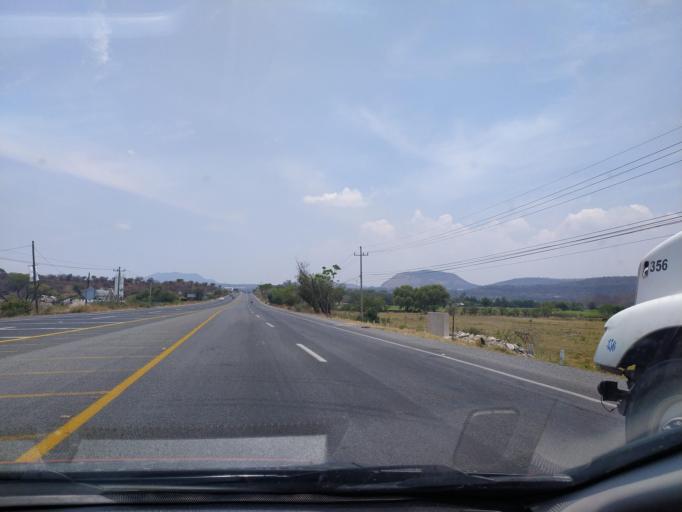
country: MX
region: Jalisco
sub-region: Acatlan de Juarez
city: Villa de los Ninos
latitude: 20.4013
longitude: -103.5935
